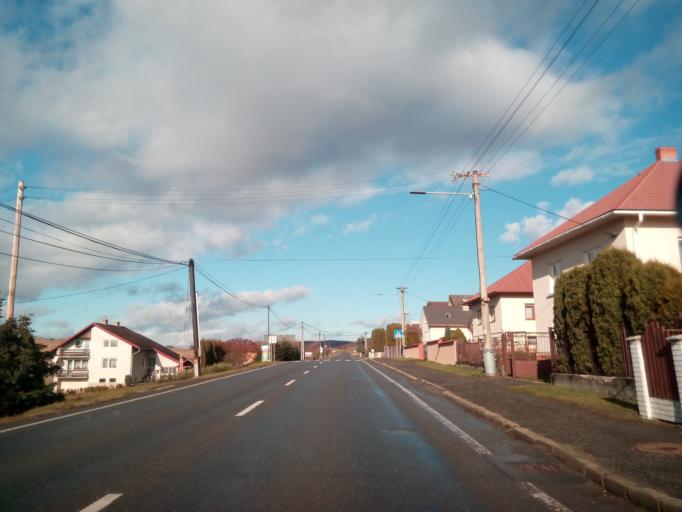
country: SK
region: Presovsky
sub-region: Okres Bardejov
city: Bardejov
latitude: 49.2181
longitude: 21.2948
